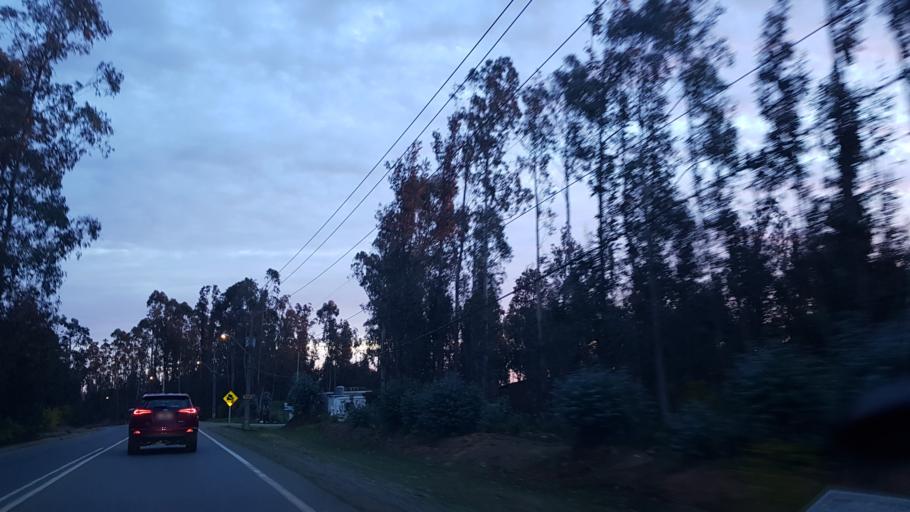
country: CL
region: Valparaiso
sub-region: Provincia de Valparaiso
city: Valparaiso
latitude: -33.0705
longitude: -71.6397
